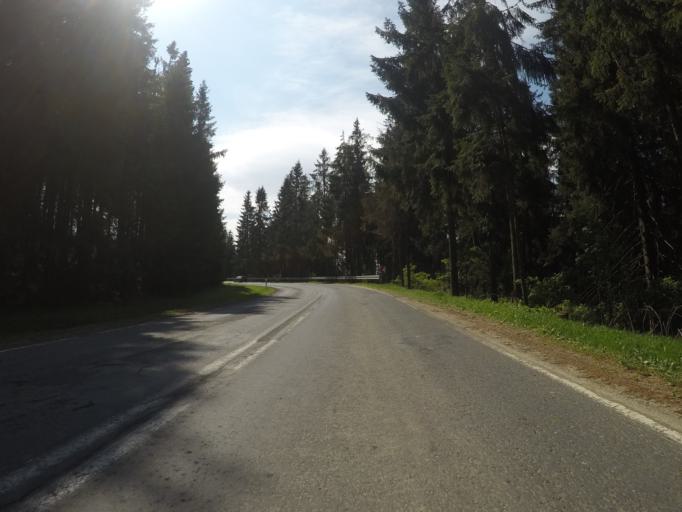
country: PL
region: Lesser Poland Voivodeship
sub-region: Powiat tatrzanski
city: Bukowina Tatrzanska
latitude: 49.3065
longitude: 20.1123
